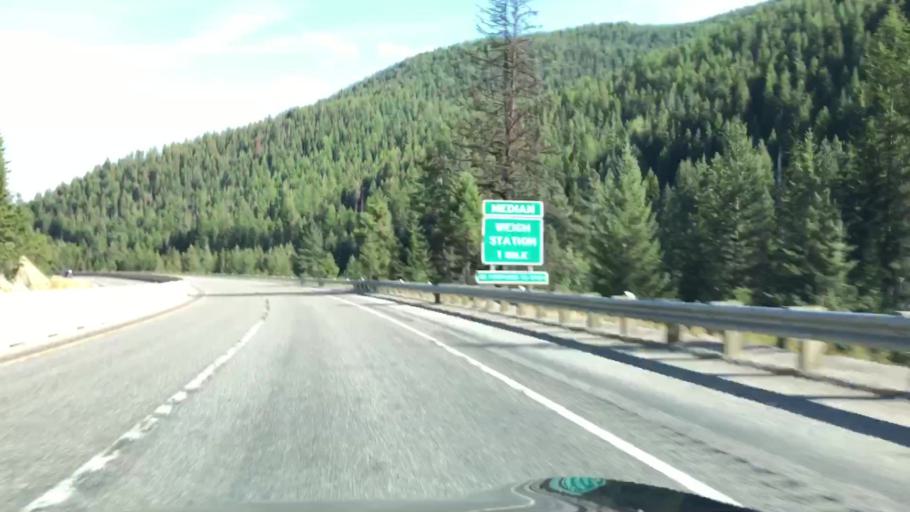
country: US
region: Montana
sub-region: Sanders County
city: Thompson Falls
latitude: 47.3950
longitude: -115.4534
